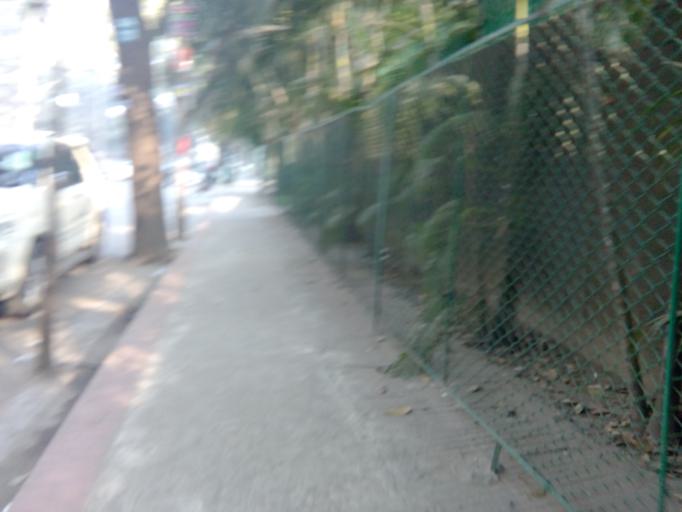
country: BD
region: Dhaka
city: Azimpur
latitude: 23.7398
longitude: 90.3807
